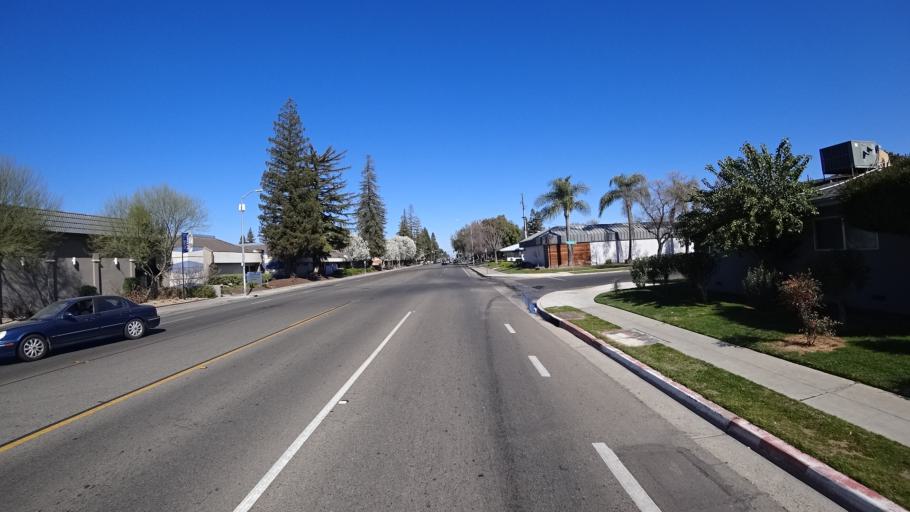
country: US
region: California
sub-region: Fresno County
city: Fresno
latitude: 36.8136
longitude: -119.7813
